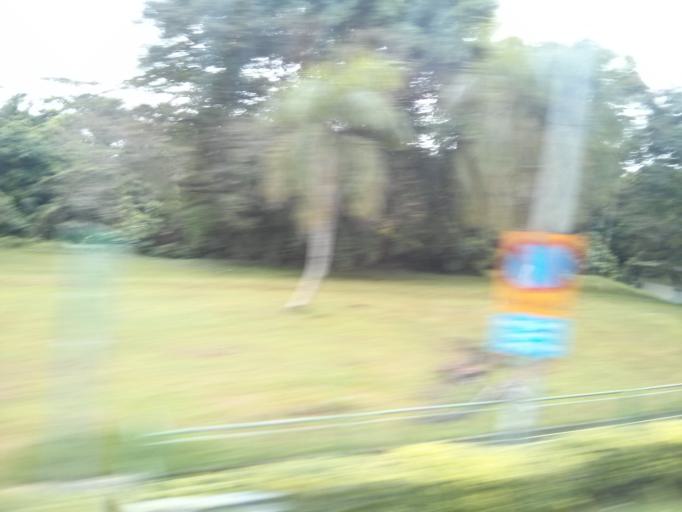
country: SG
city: Singapore
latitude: 1.2872
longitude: 103.7962
